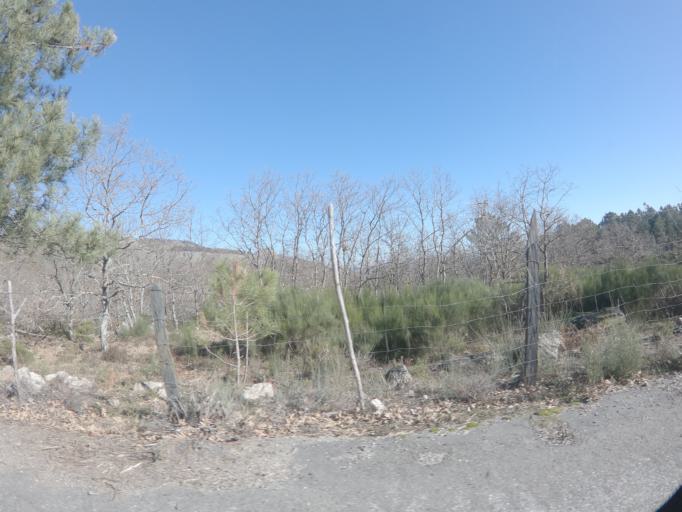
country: PT
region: Vila Real
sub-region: Vila Real
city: Vila Real
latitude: 41.3314
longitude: -7.7866
